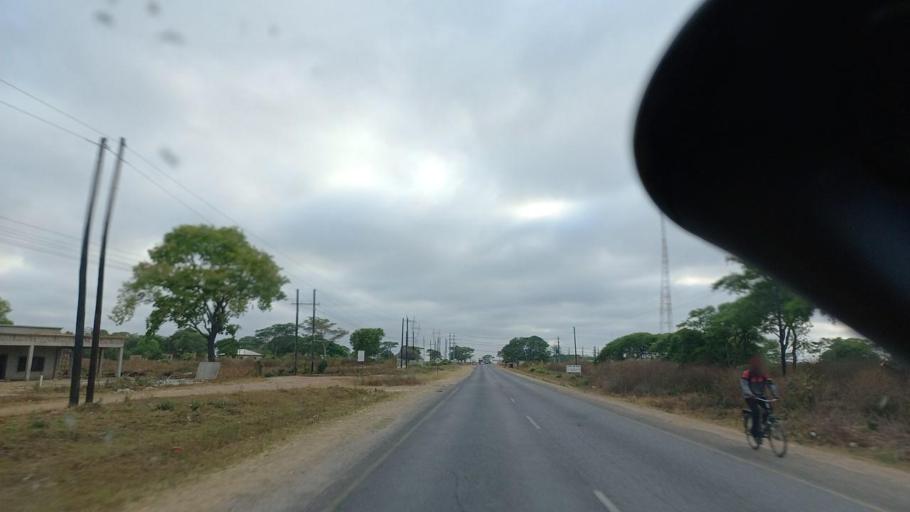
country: ZM
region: Lusaka
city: Chongwe
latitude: -15.3443
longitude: 28.5127
